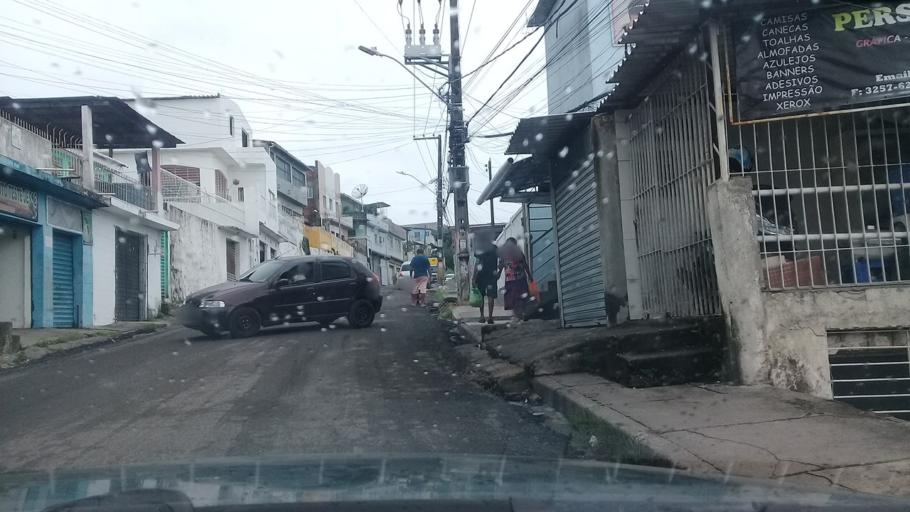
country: BR
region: Pernambuco
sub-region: Jaboatao Dos Guararapes
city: Jaboatao dos Guararapes
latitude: -8.0876
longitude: -34.9749
